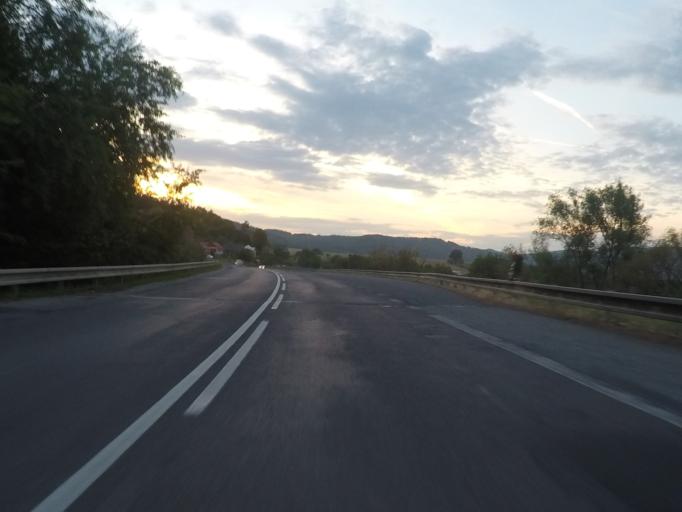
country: SK
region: Banskobystricky
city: Rimavska Sobota
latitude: 48.4758
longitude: 19.9491
